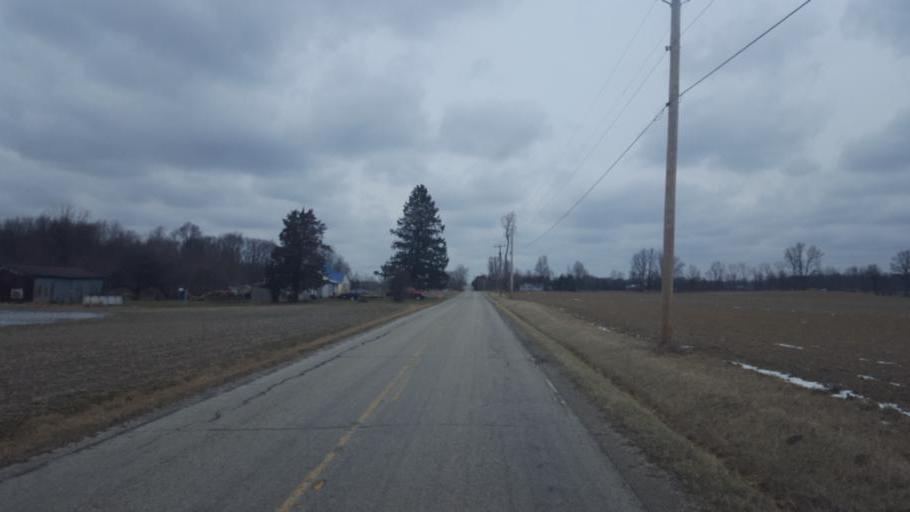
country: US
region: Ohio
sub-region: Crawford County
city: Crestline
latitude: 40.7441
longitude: -82.6978
